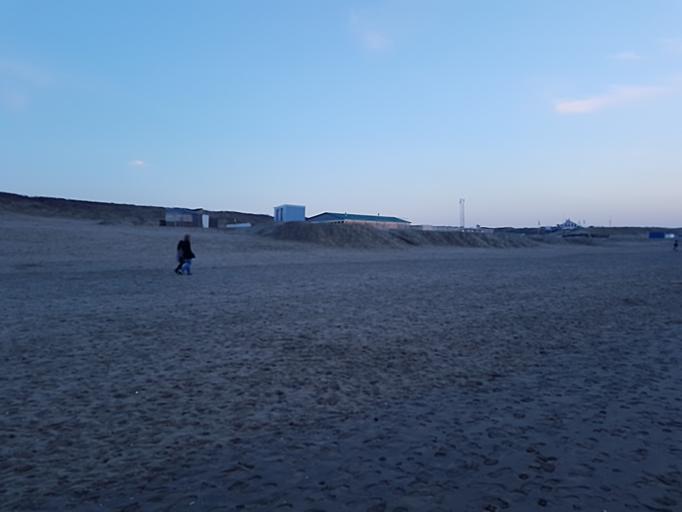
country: NL
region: South Holland
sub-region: Gemeente Wassenaar
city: Wassenaar
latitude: 52.1655
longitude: 4.3497
